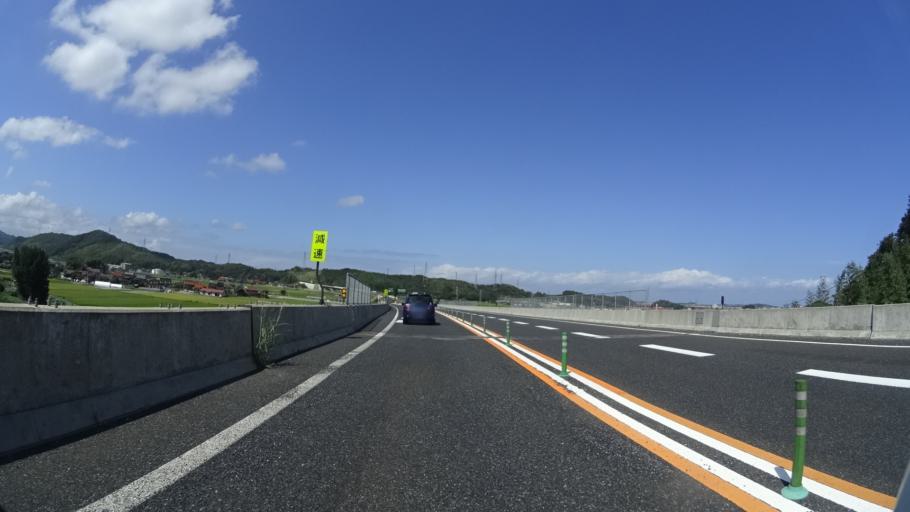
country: JP
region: Tottori
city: Tottori
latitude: 35.4898
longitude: 134.1963
